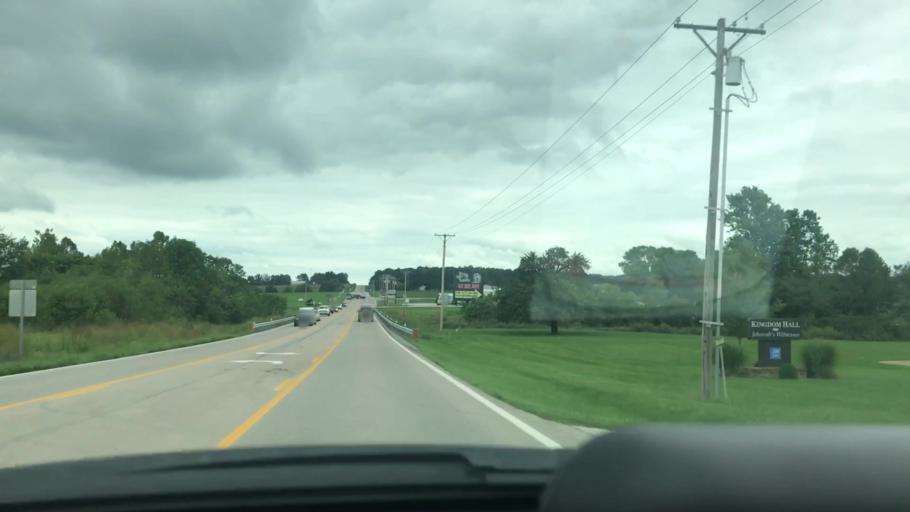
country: US
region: Missouri
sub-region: Dallas County
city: Buffalo
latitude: 37.6632
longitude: -93.1035
